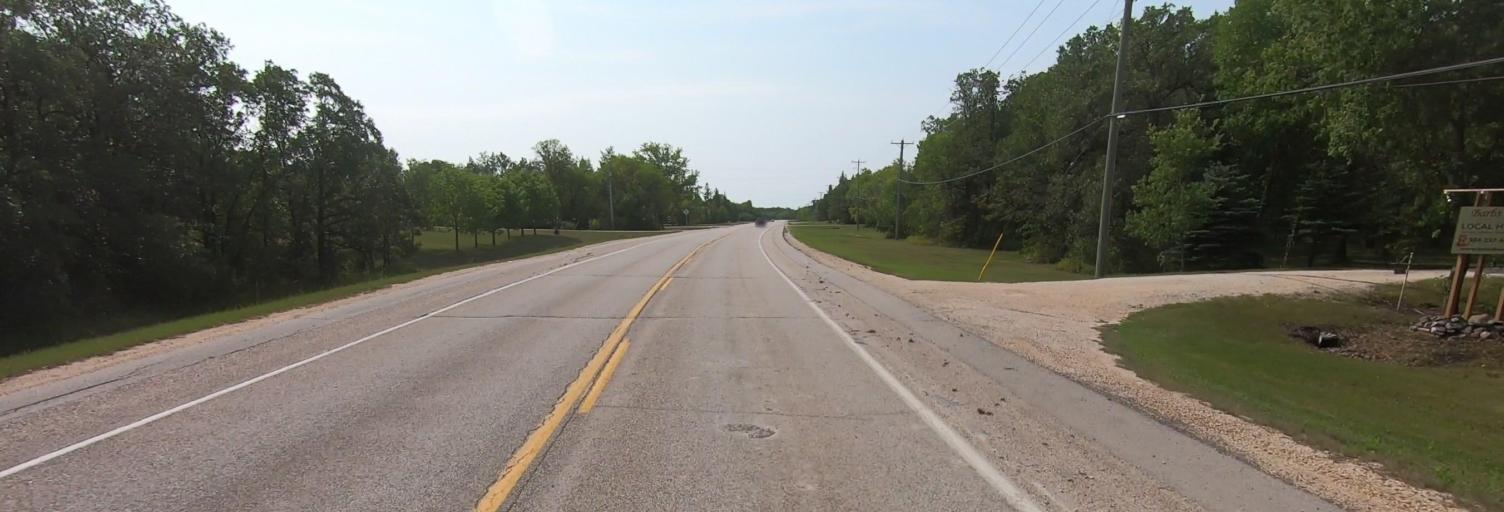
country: CA
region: Manitoba
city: Niverville
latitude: 49.7173
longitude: -97.0902
